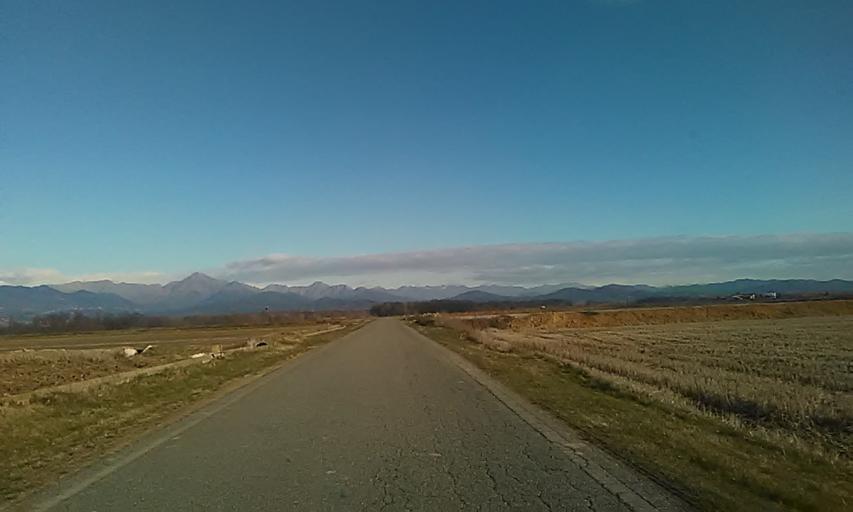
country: IT
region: Piedmont
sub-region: Provincia di Vercelli
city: Rovasenda
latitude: 45.5346
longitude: 8.2747
